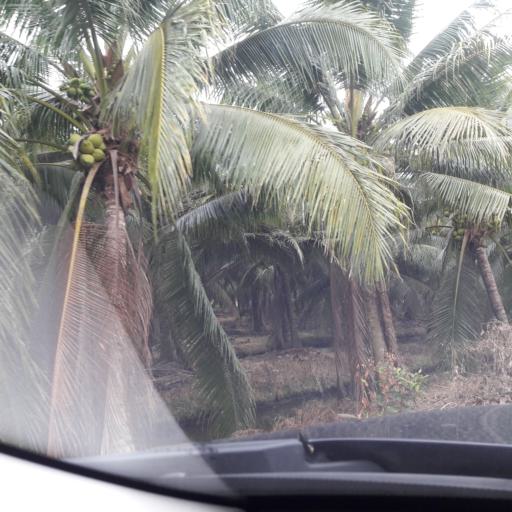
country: TH
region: Ratchaburi
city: Damnoen Saduak
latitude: 13.5849
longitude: 99.9418
